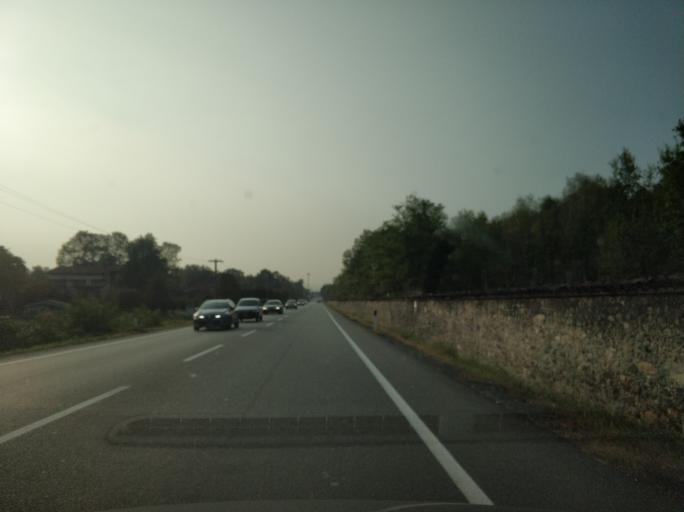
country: IT
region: Piedmont
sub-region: Provincia di Torino
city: Robassomero
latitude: 45.1982
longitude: 7.5587
